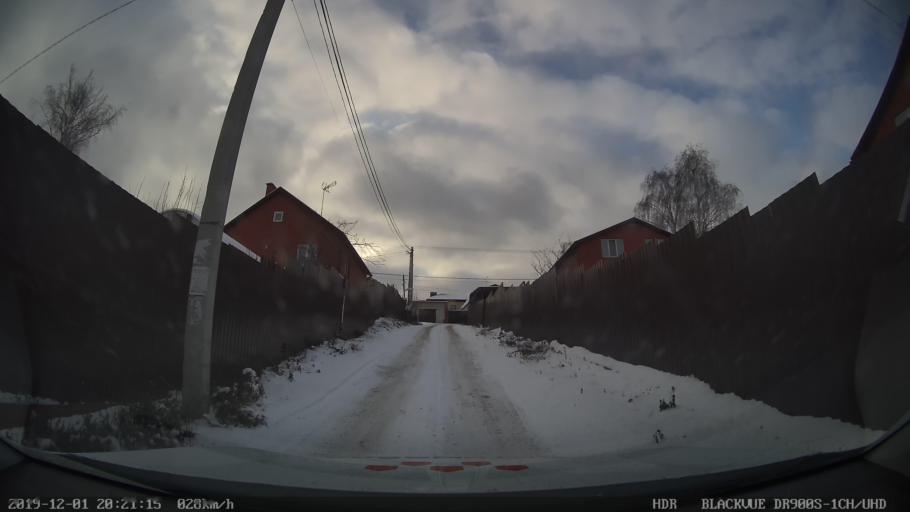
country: RU
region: Tatarstan
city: Stolbishchi
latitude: 55.7444
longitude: 49.2700
